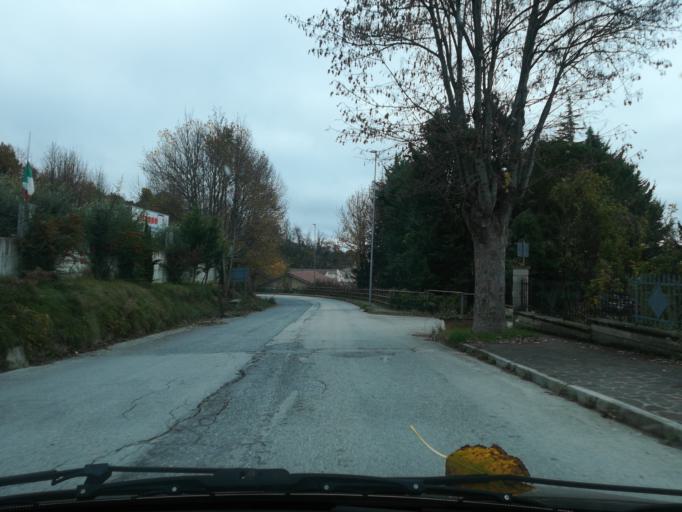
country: IT
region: Molise
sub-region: Provincia di Isernia
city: Agnone
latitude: 41.8155
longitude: 14.3733
